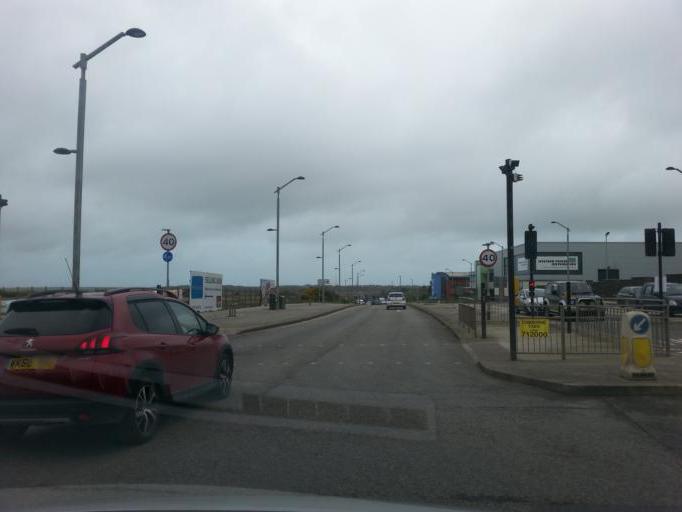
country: GB
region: England
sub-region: Cornwall
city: Camborne
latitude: 50.2251
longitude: -5.2775
